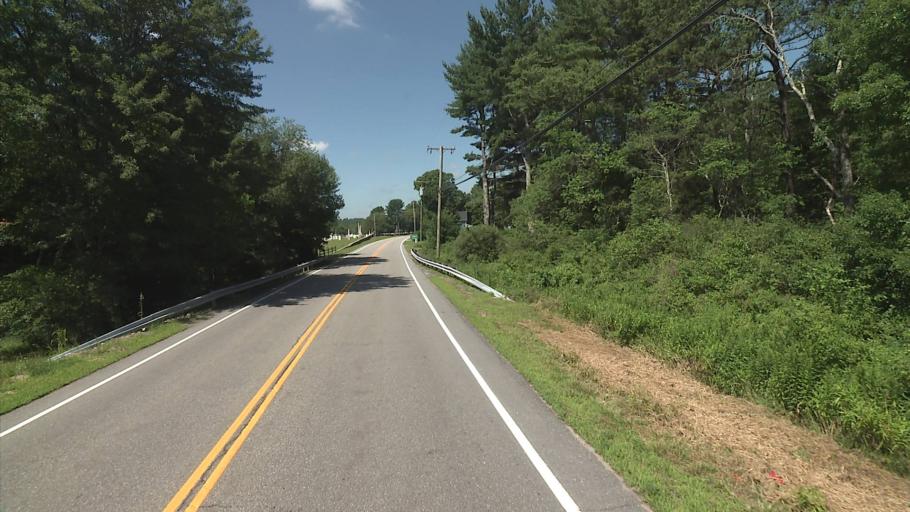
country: US
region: Connecticut
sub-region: Windham County
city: Moosup
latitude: 41.6949
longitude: -71.8011
